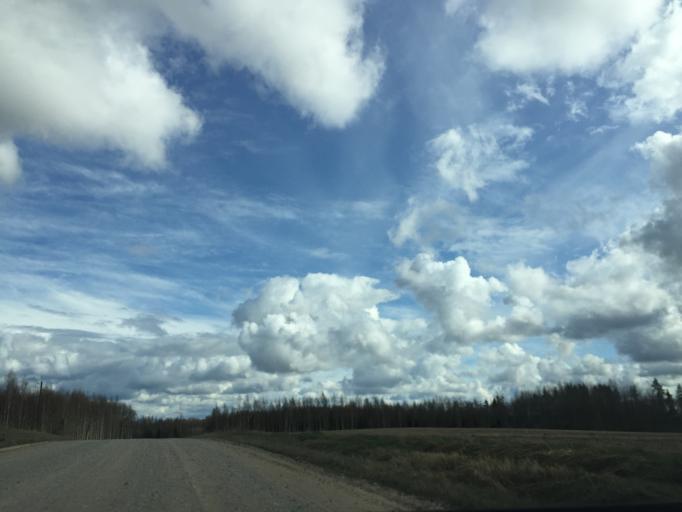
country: LV
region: Limbazu Rajons
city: Limbazi
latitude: 57.6050
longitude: 24.7979
